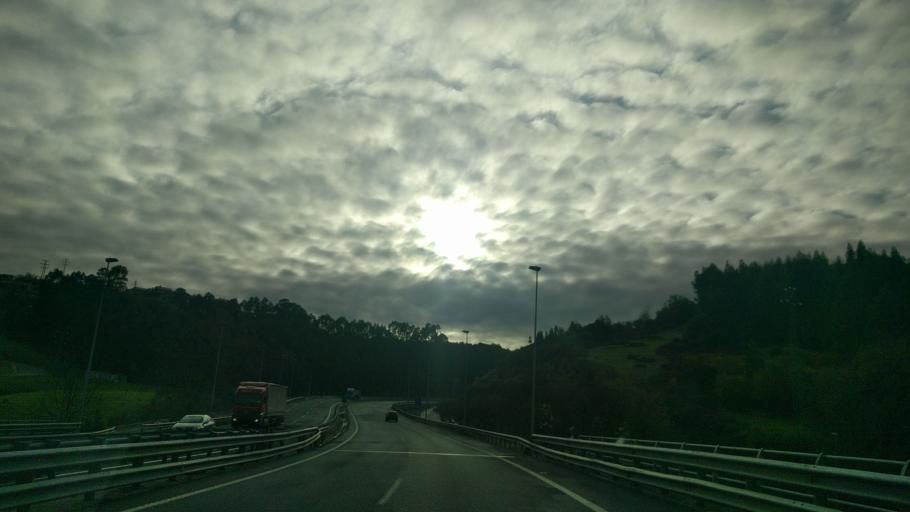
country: ES
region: Cantabria
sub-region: Provincia de Cantabria
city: Castro-Urdiales
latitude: 43.3661
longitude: -3.2202
